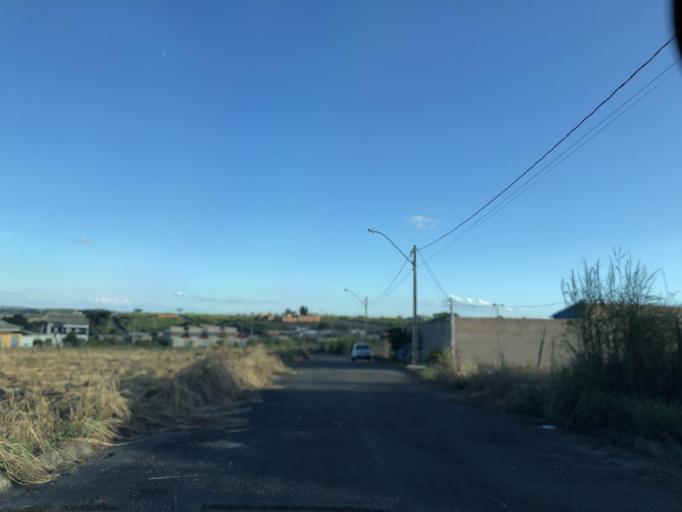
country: BR
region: Goias
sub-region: Luziania
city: Luziania
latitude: -16.2647
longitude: -47.9702
